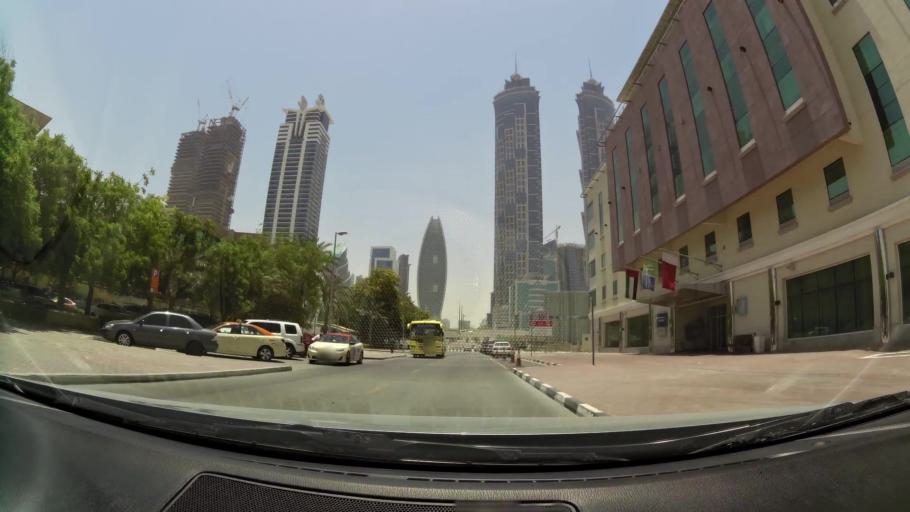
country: AE
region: Dubai
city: Dubai
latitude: 25.1890
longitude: 55.2551
